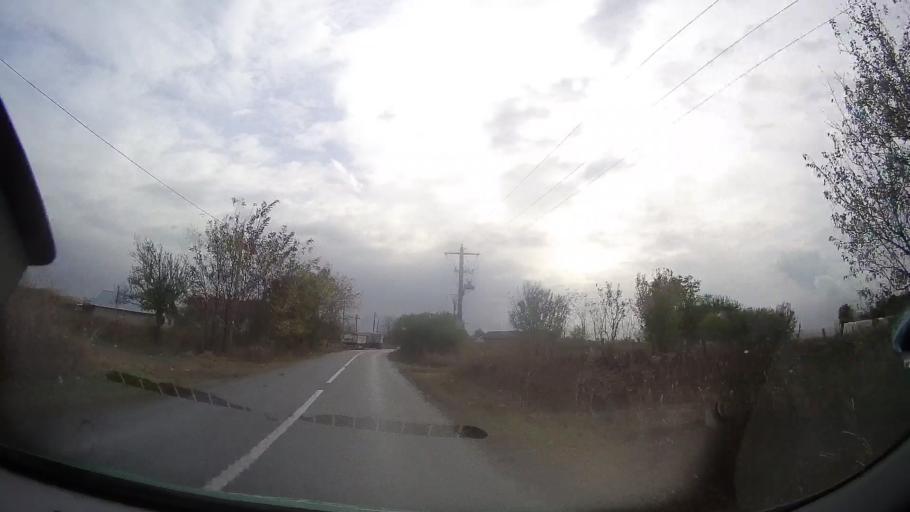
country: RO
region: Ialomita
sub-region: Comuna Fierbinti-Targ
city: Fierbintii de Jos
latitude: 44.7014
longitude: 26.3935
